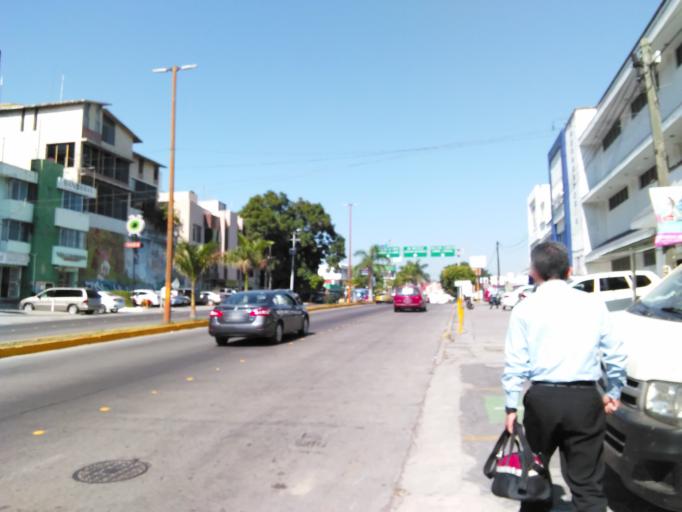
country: MX
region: Nayarit
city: Tepic
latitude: 21.4961
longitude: -104.8969
